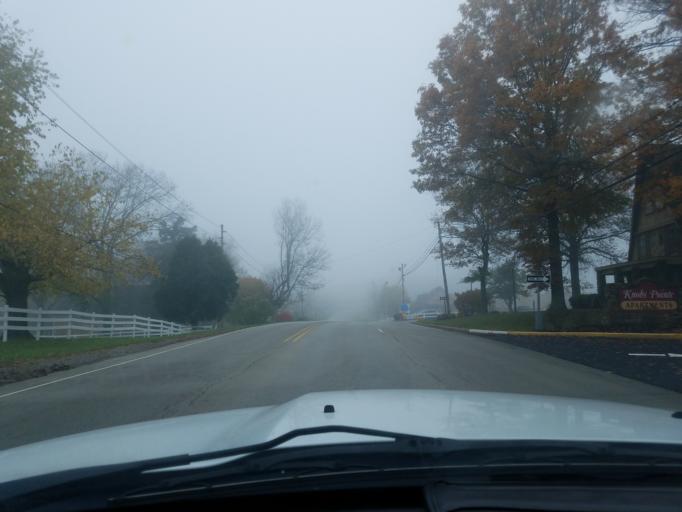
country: US
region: Indiana
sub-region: Floyd County
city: New Albany
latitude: 38.3141
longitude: -85.8513
